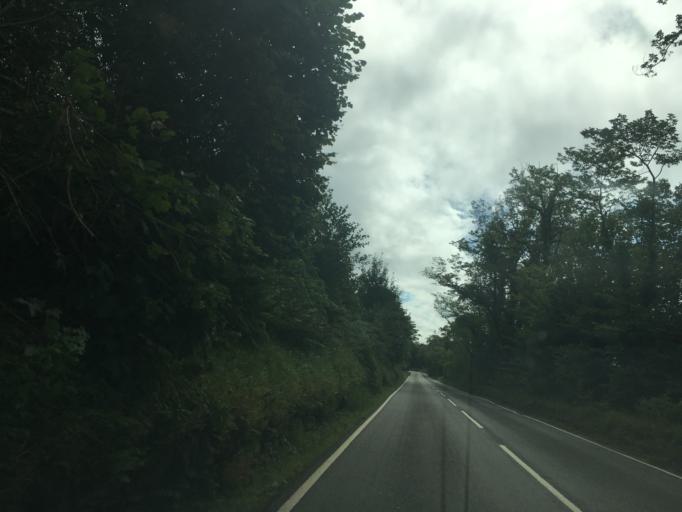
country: GB
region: Scotland
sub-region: Argyll and Bute
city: Lochgilphead
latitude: 56.1247
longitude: -5.4895
